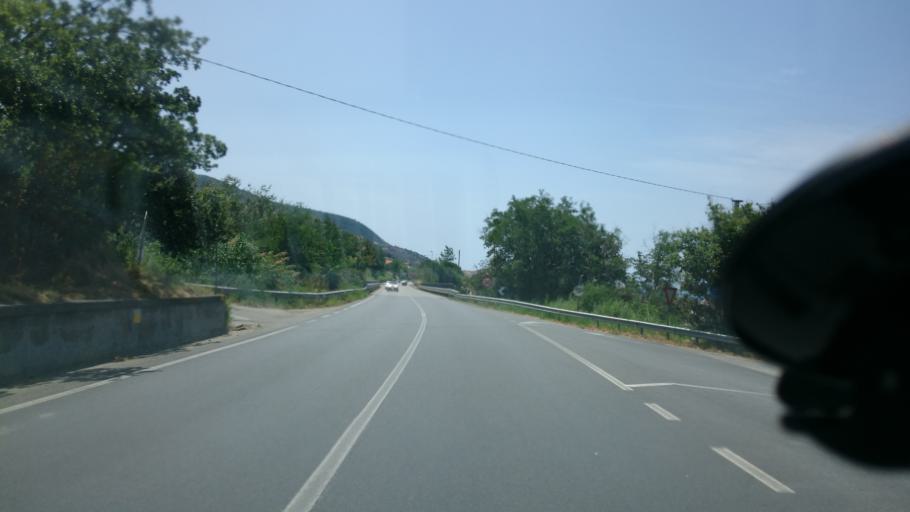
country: IT
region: Calabria
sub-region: Provincia di Cosenza
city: Cittadella del Capo
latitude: 39.5787
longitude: 15.8695
